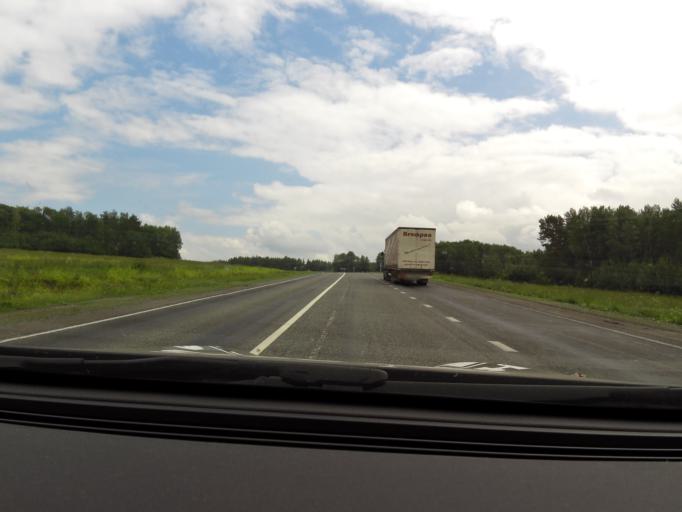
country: RU
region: Perm
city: Suksun
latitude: 57.0946
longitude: 57.3244
